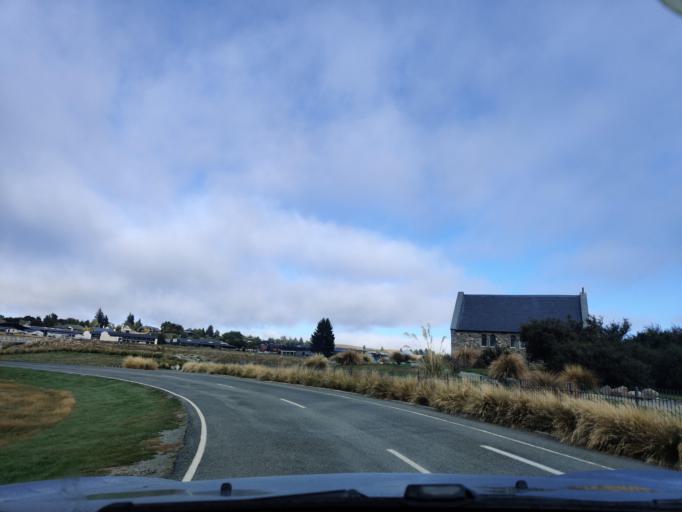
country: NZ
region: Canterbury
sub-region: Timaru District
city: Pleasant Point
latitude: -44.0034
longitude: 170.4830
